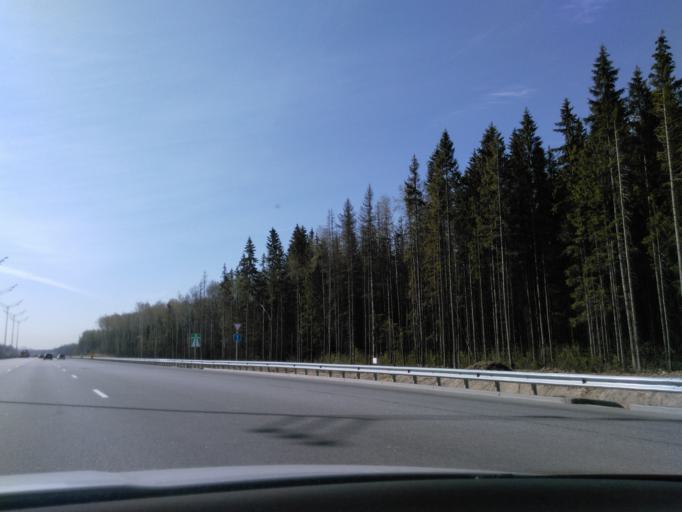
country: RU
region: Moskovskaya
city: Rzhavki
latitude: 56.0061
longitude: 37.2899
